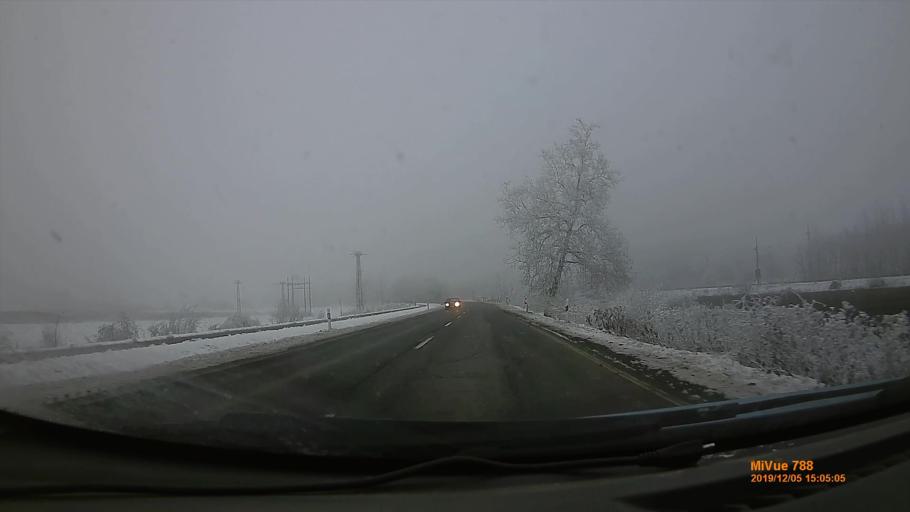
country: HU
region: Szabolcs-Szatmar-Bereg
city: Tiszanagyfalu
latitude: 48.1056
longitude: 21.4897
